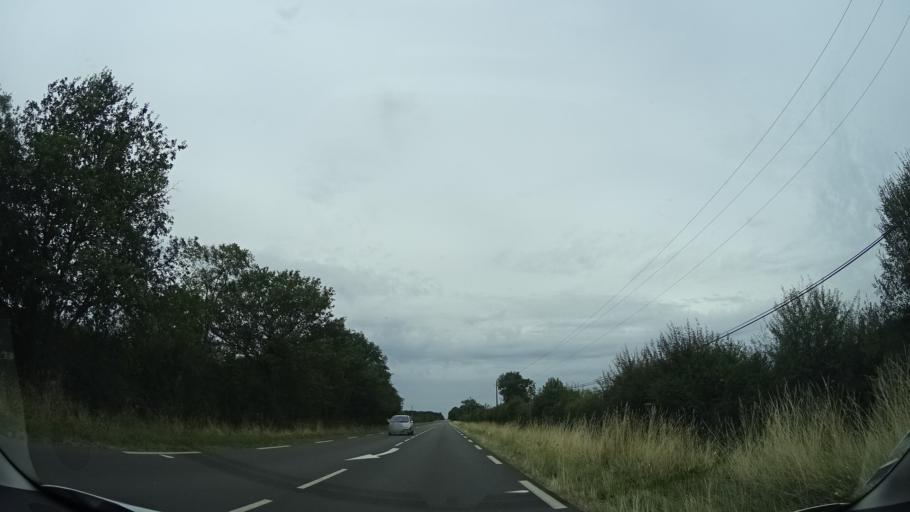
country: FR
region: Pays de la Loire
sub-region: Departement de la Mayenne
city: Meslay-du-Maine
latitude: 47.9769
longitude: -0.6024
